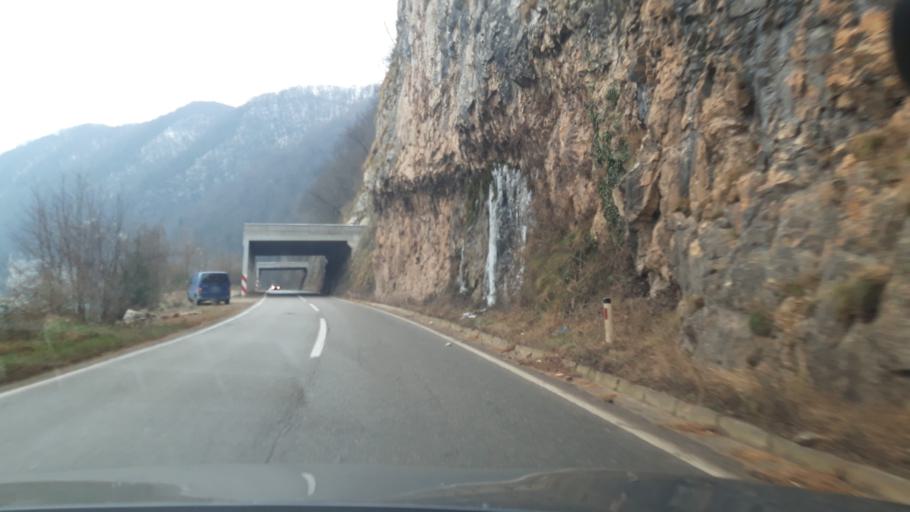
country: RS
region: Central Serbia
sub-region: Macvanski Okrug
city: Mali Zvornik
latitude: 44.3434
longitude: 19.1137
